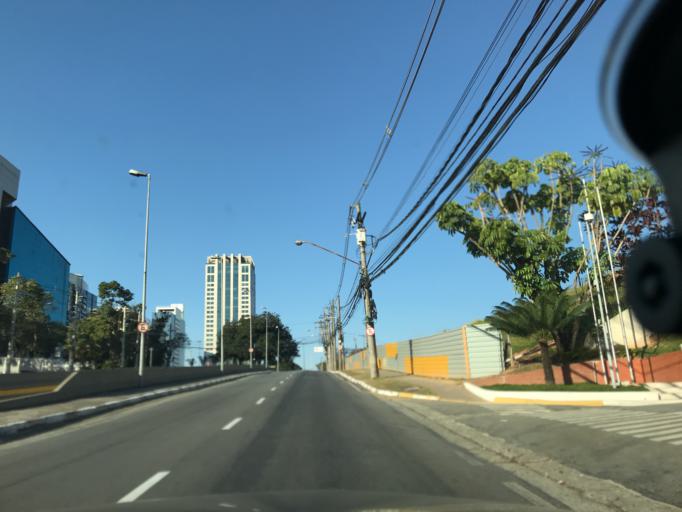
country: BR
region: Sao Paulo
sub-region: Carapicuiba
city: Carapicuiba
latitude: -23.4990
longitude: -46.8503
